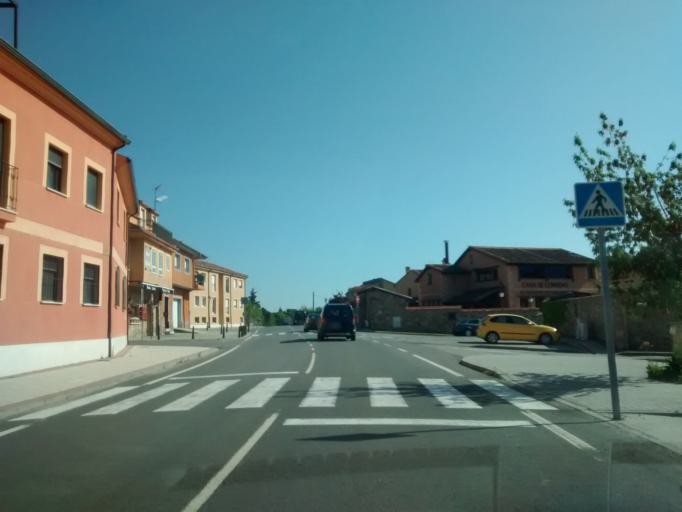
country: ES
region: Castille and Leon
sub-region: Provincia de Segovia
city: Torrecaballeros
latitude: 40.9914
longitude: -4.0231
